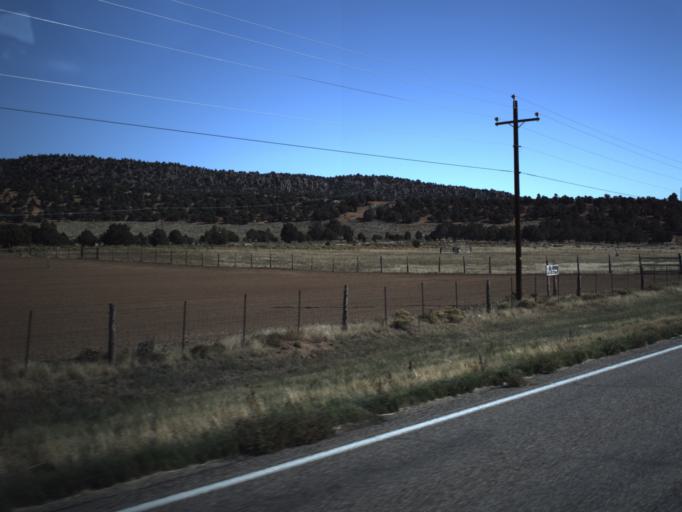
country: US
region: Utah
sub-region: Iron County
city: Cedar City
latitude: 37.6320
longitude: -113.2990
